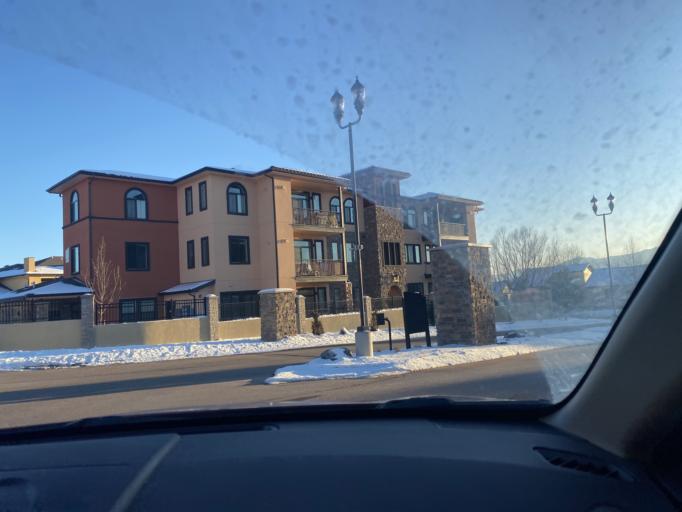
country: US
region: Colorado
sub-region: El Paso County
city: Black Forest
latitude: 38.9657
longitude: -104.7443
